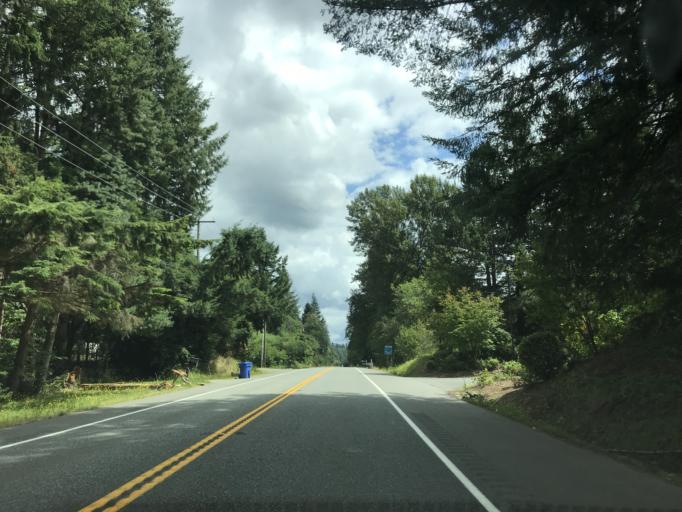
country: US
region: Washington
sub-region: King County
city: Maple Heights-Lake Desire
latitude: 47.4229
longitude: -122.0953
